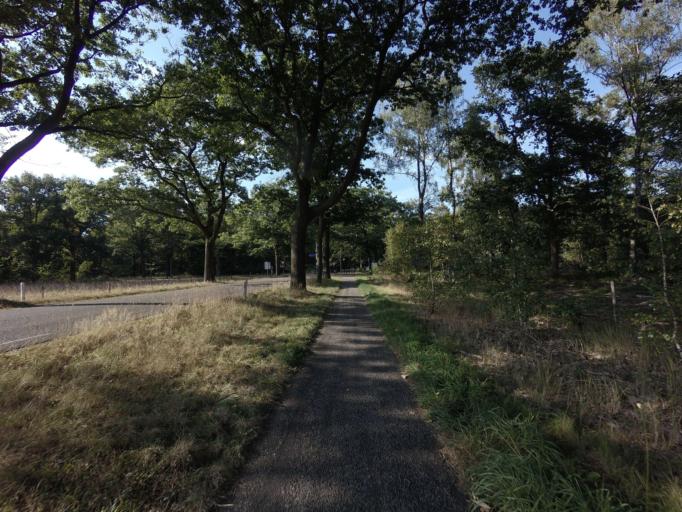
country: NL
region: North Brabant
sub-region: Gemeente Heeze-Leende
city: Heeze
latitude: 51.3781
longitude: 5.6239
